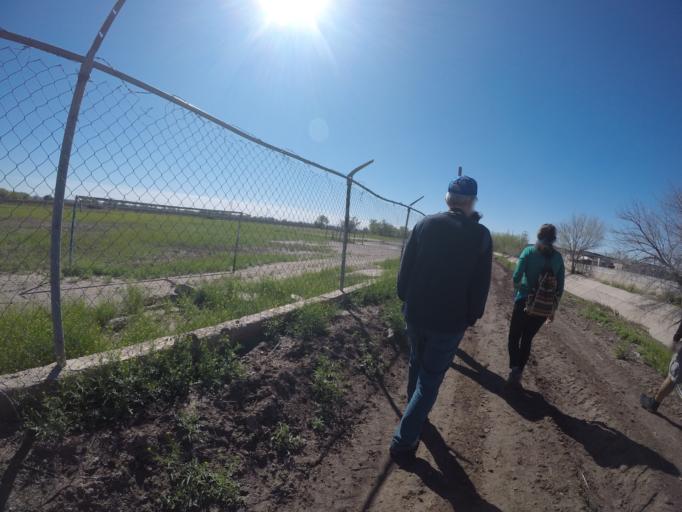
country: US
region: Texas
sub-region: El Paso County
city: Socorro
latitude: 31.6388
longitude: -106.3350
